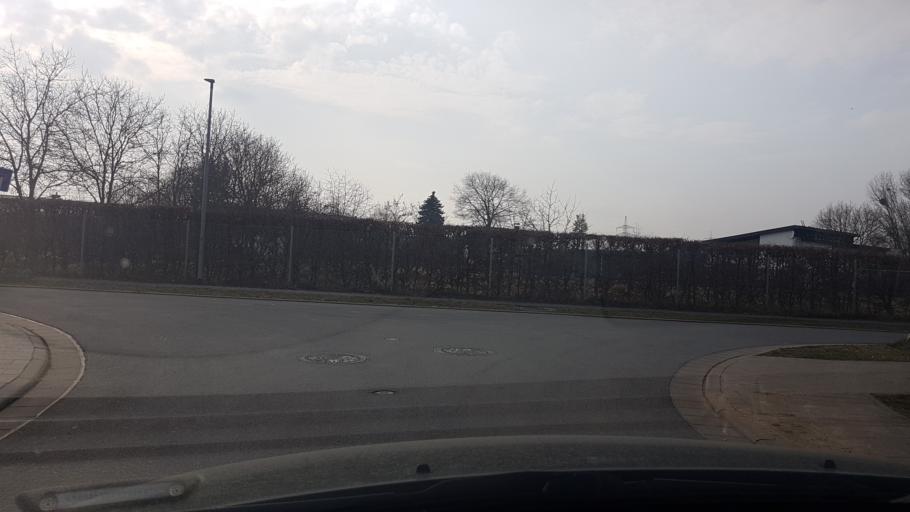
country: DE
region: Bavaria
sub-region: Upper Franconia
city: Hallstadt
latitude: 49.9253
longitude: 10.8673
